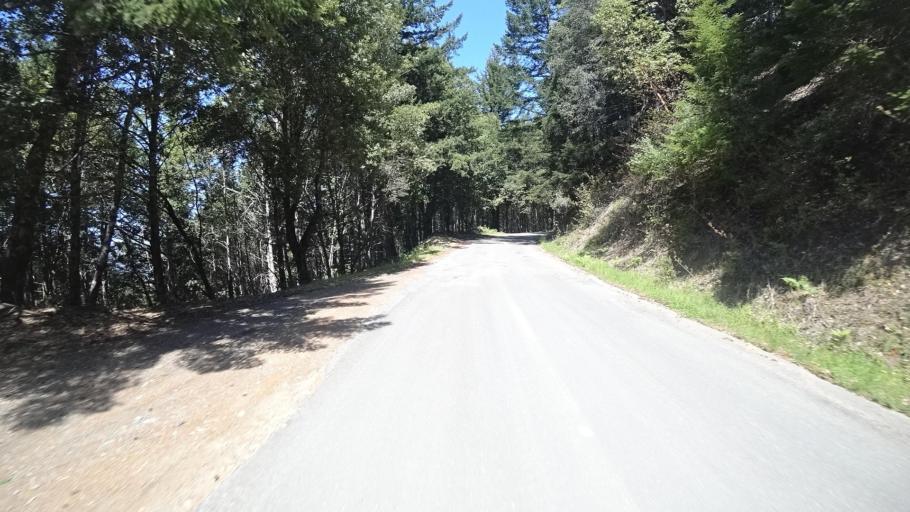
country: US
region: California
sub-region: Humboldt County
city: Rio Dell
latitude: 40.2642
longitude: -124.0937
